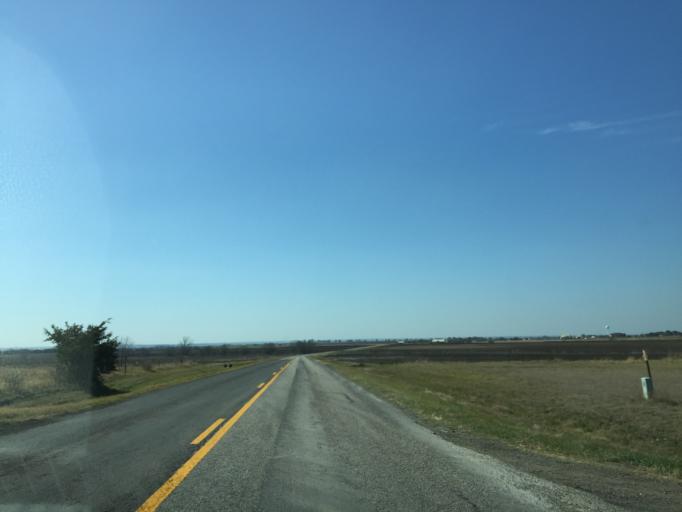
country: US
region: Texas
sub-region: Williamson County
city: Serenada
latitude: 30.7081
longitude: -97.5814
